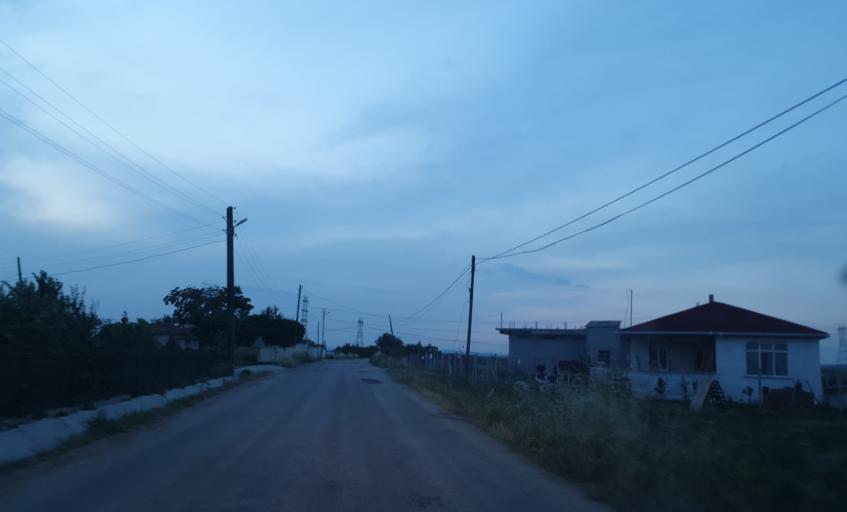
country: TR
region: Kirklareli
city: Vize
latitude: 41.4897
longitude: 27.7523
